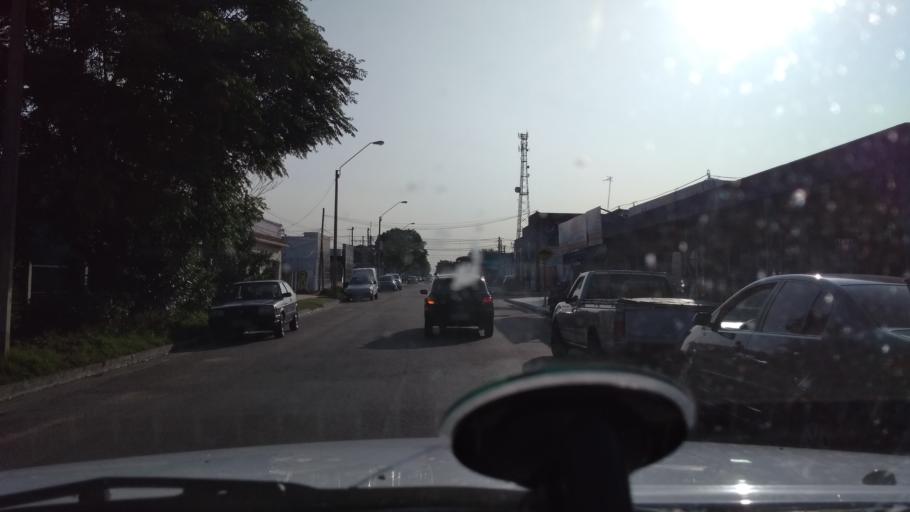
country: UY
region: Canelones
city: Santa Rosa
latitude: -34.4970
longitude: -56.0353
